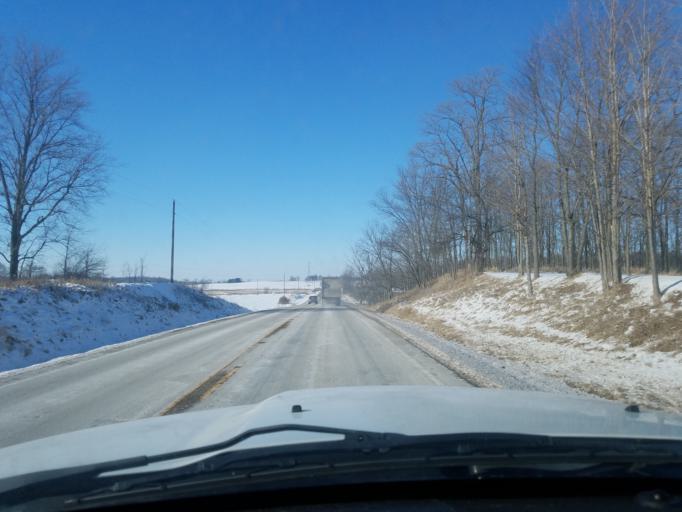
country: US
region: Indiana
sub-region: Noble County
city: Avilla
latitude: 41.3945
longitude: -85.2655
